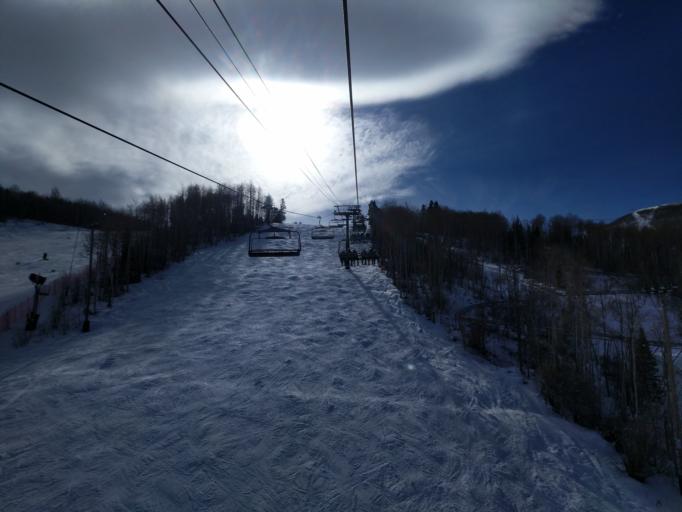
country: US
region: Utah
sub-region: Summit County
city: Park City
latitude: 40.6468
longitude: -111.5081
